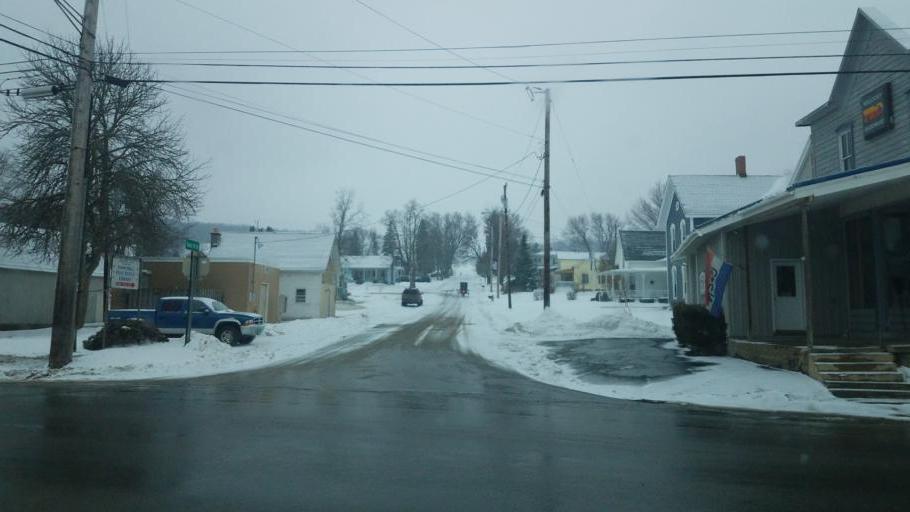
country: US
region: New York
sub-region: Steuben County
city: Canisteo
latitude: 42.1227
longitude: -77.5032
